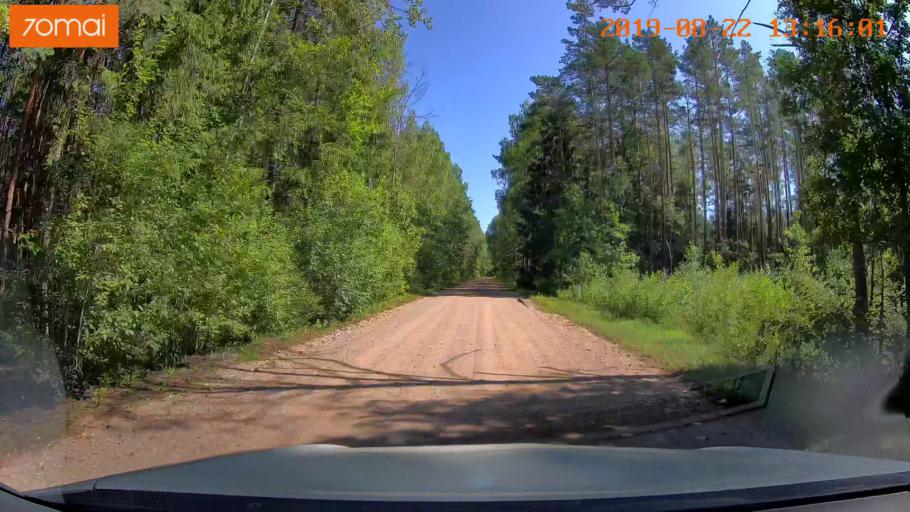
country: BY
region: Minsk
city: Prawdzinski
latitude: 53.2575
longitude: 27.9056
